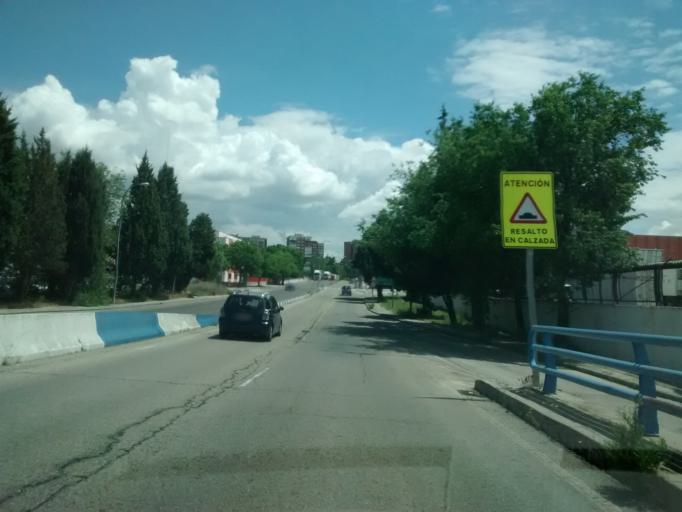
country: ES
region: Madrid
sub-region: Provincia de Madrid
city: Coslada
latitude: 40.4317
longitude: -3.5533
